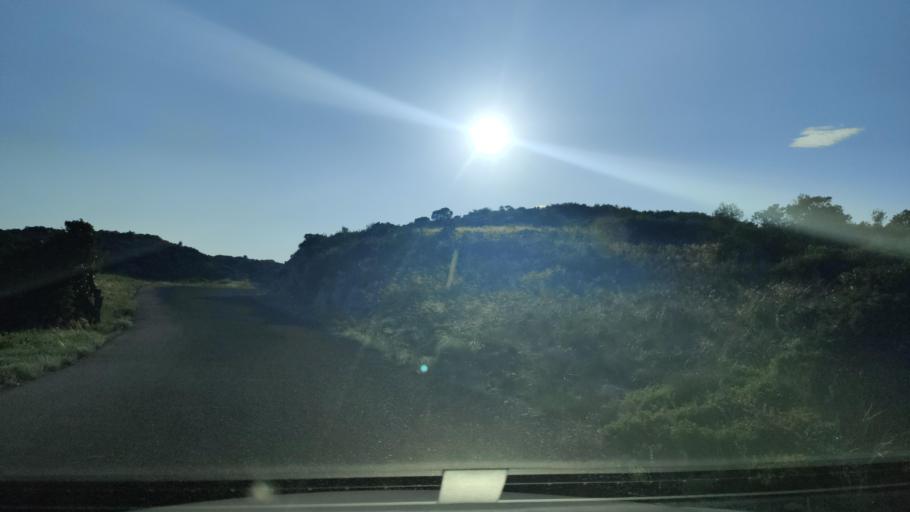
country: FR
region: Languedoc-Roussillon
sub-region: Departement des Pyrenees-Orientales
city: Estagel
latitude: 42.7861
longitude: 2.7505
